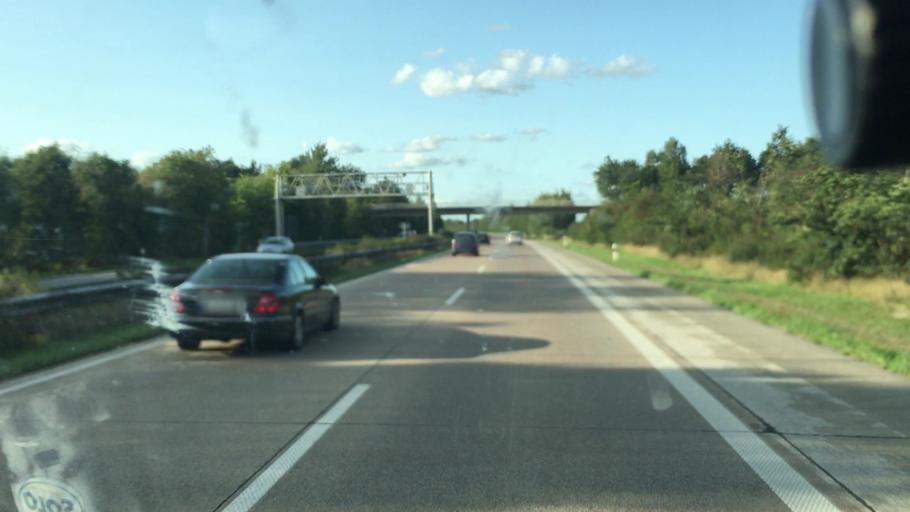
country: DE
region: Lower Saxony
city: Wiefelstede
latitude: 53.3038
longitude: 8.1454
